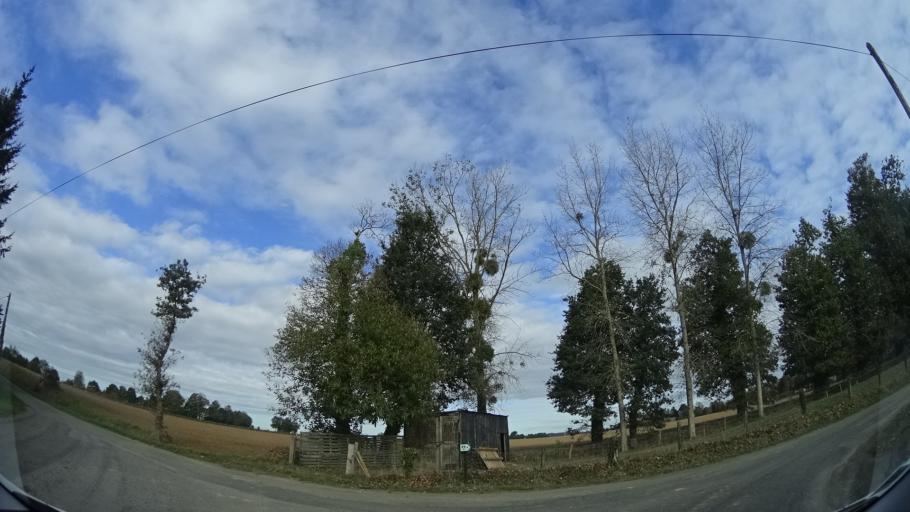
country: FR
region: Brittany
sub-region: Departement d'Ille-et-Vilaine
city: Vignoc
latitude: 48.2416
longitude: -1.8025
